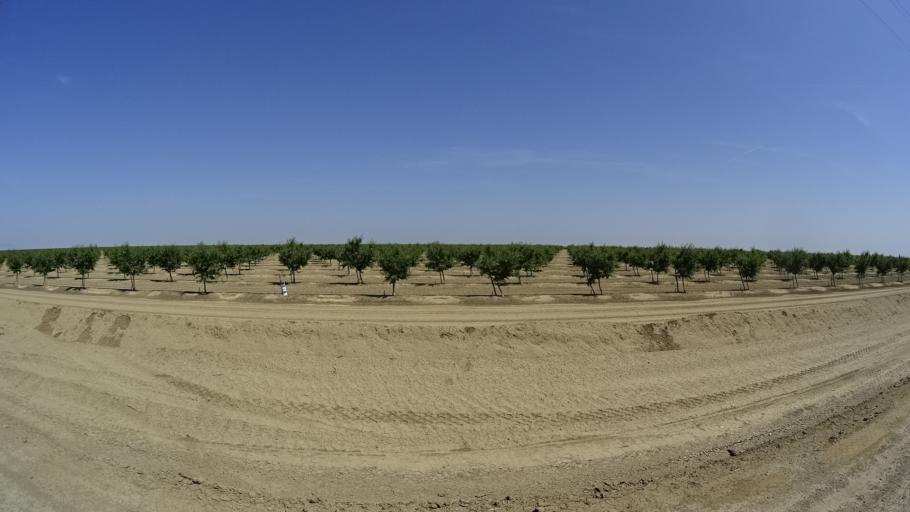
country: US
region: California
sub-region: Kings County
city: Kettleman City
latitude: 36.0943
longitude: -119.9776
